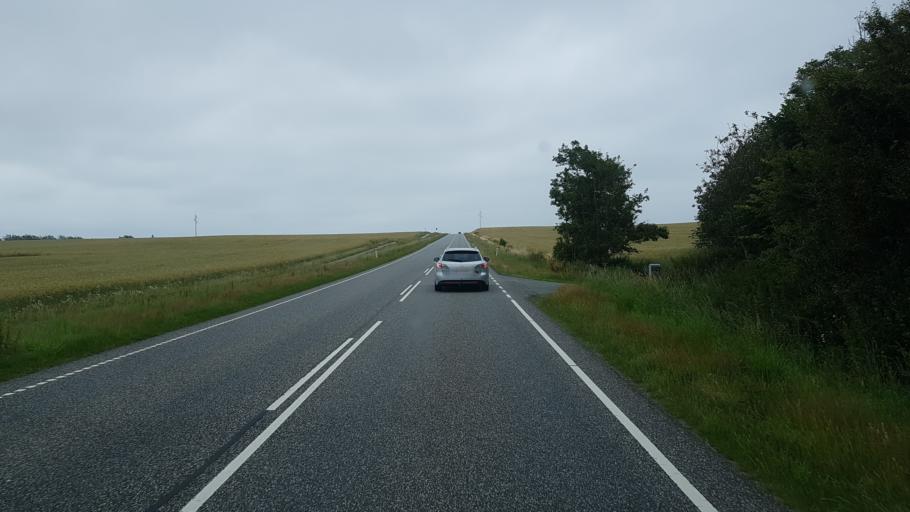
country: DK
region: Central Jutland
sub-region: Struer Kommune
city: Struer
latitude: 56.5144
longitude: 8.5572
